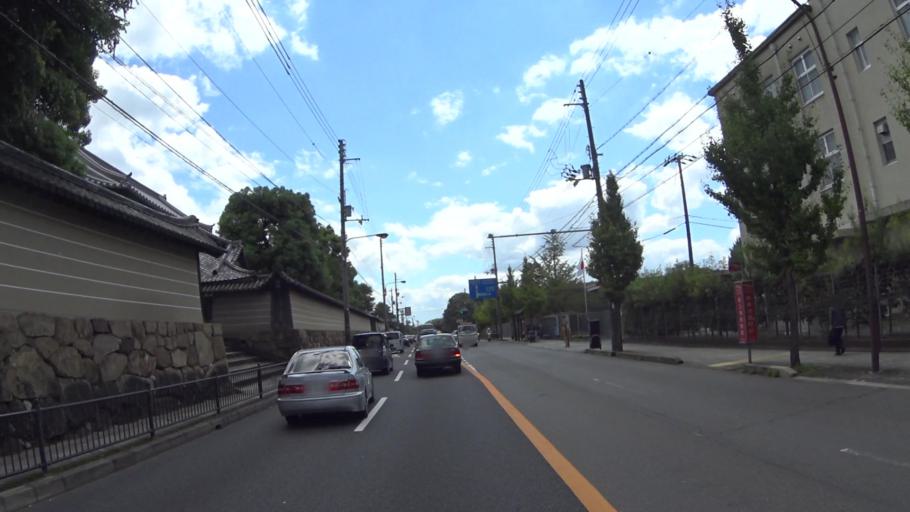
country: JP
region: Kyoto
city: Kyoto
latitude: 34.9907
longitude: 135.7746
